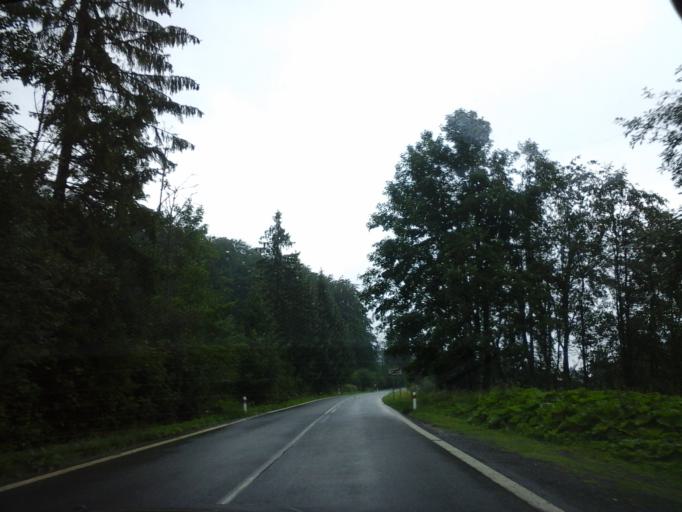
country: PL
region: Lesser Poland Voivodeship
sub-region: Powiat tatrzanski
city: Bukowina Tatrzanska
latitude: 49.2659
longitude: 20.1406
